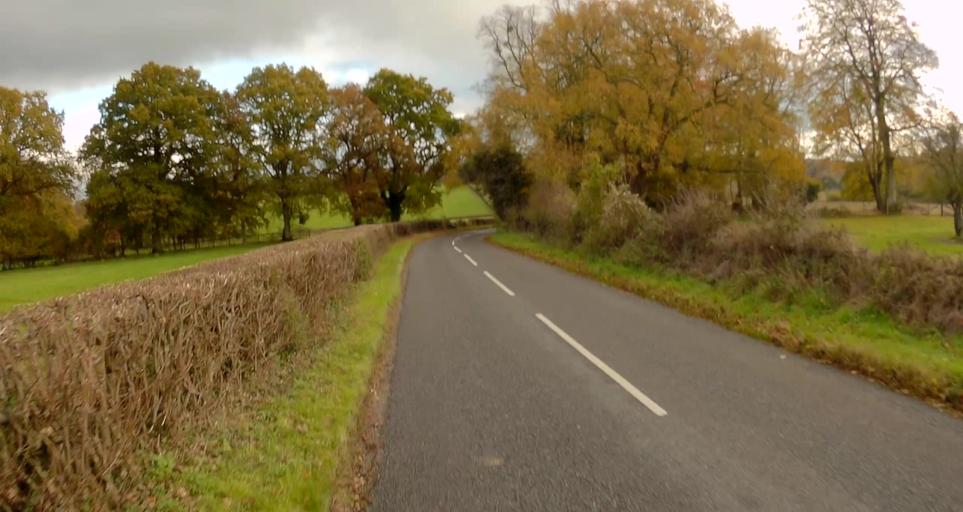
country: GB
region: England
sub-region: Hampshire
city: Old Basing
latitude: 51.2381
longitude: -1.0322
